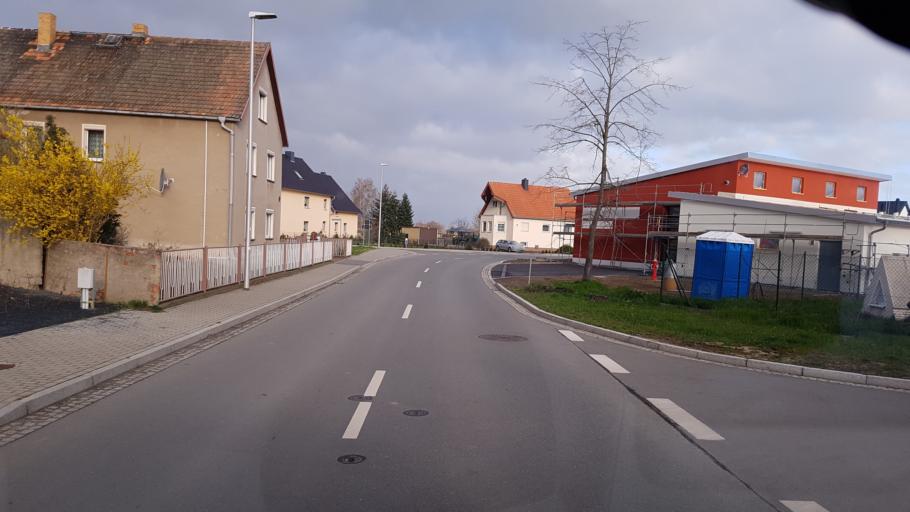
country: DE
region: Saxony
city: Nauwalde
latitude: 51.4174
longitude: 13.4101
